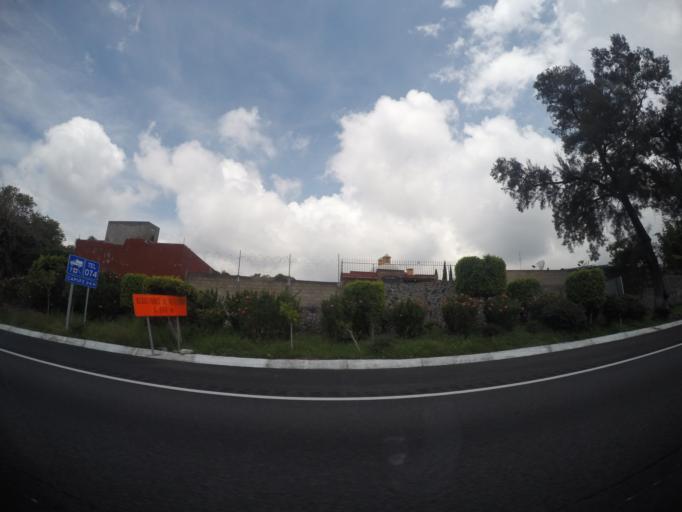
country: MX
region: Morelos
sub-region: Cuernavaca
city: Fraccionamiento Lomas de Ahuatlan
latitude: 18.9774
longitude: -99.2315
